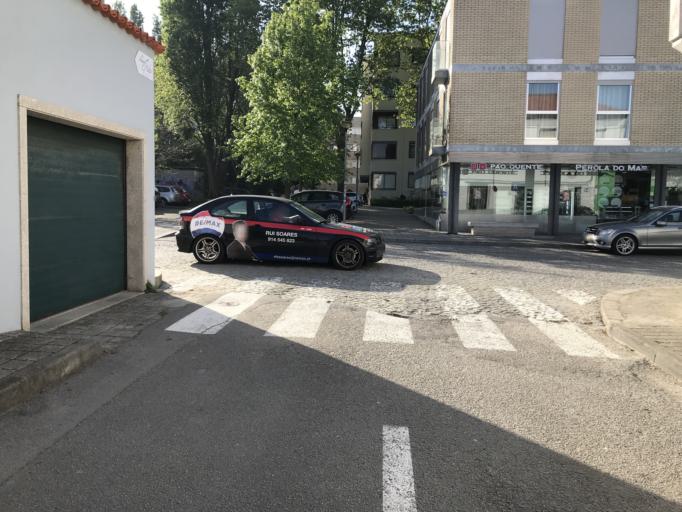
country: PT
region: Porto
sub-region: Matosinhos
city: Guifoes
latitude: 41.1825
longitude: -8.6700
